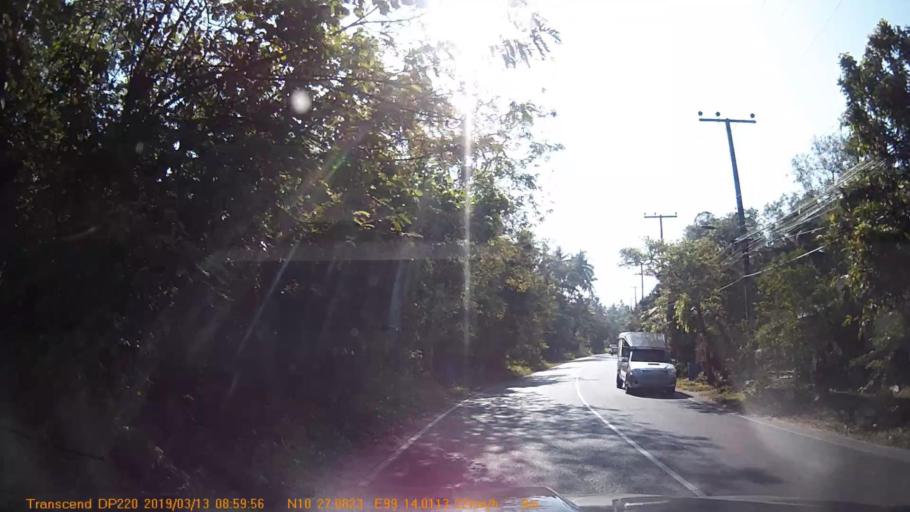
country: TH
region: Chumphon
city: Chumphon
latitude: 10.4512
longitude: 99.2340
